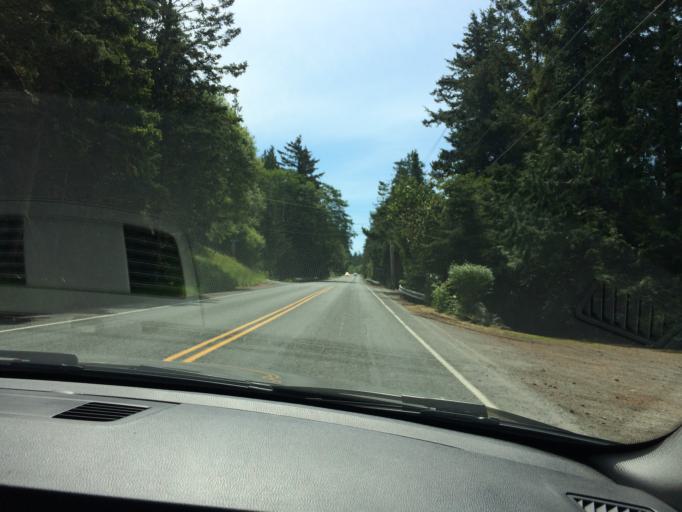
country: US
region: Washington
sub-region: Skagit County
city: Anacortes
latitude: 48.4723
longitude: -122.6548
